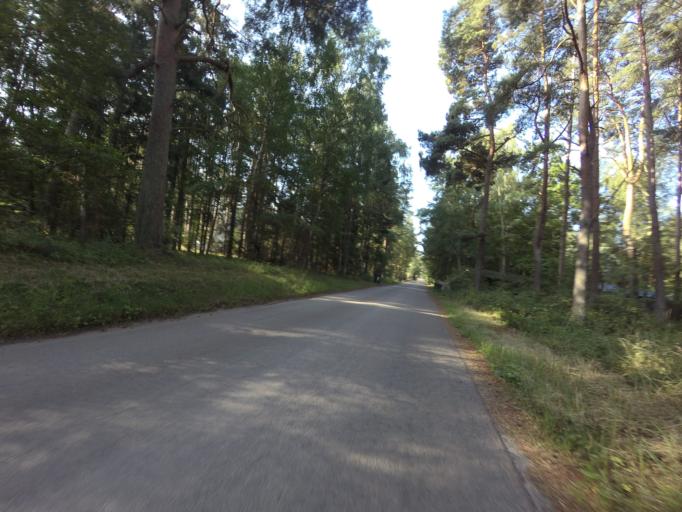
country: SE
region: Skane
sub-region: Landskrona
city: Asmundtorp
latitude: 55.8396
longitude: 12.9322
